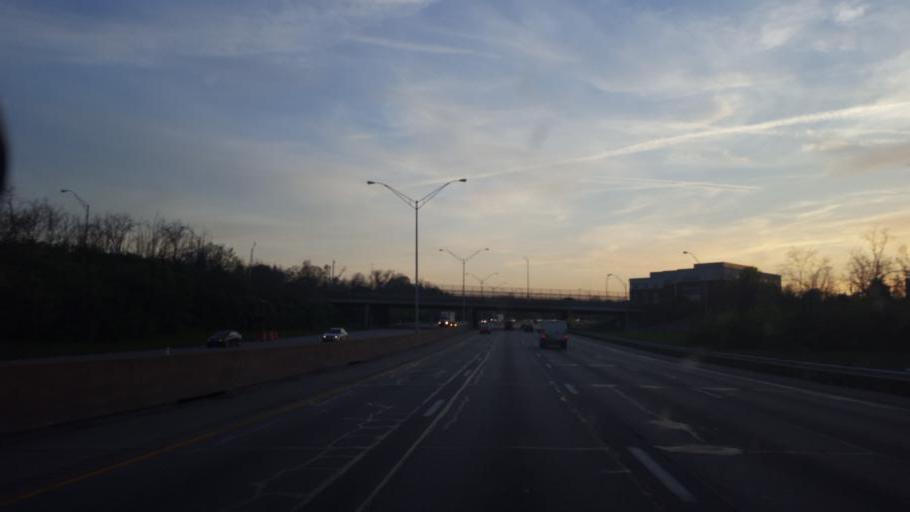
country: US
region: Ohio
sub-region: Hamilton County
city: Norwood
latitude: 39.1457
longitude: -84.4558
